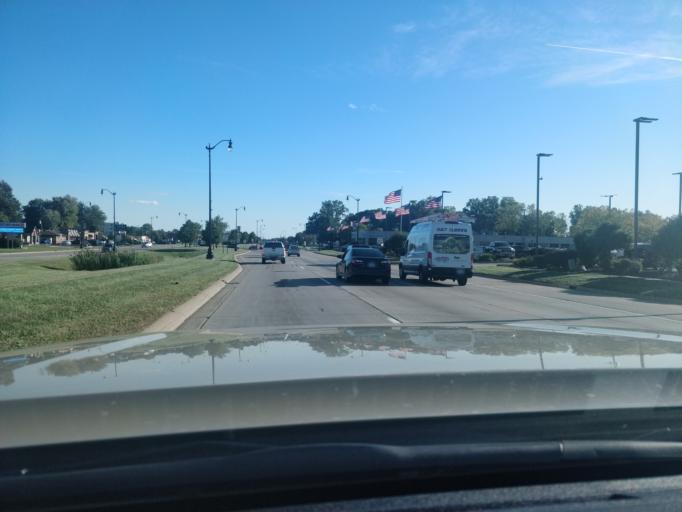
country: US
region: Michigan
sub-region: Wayne County
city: Taylor
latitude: 42.2188
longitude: -83.2690
